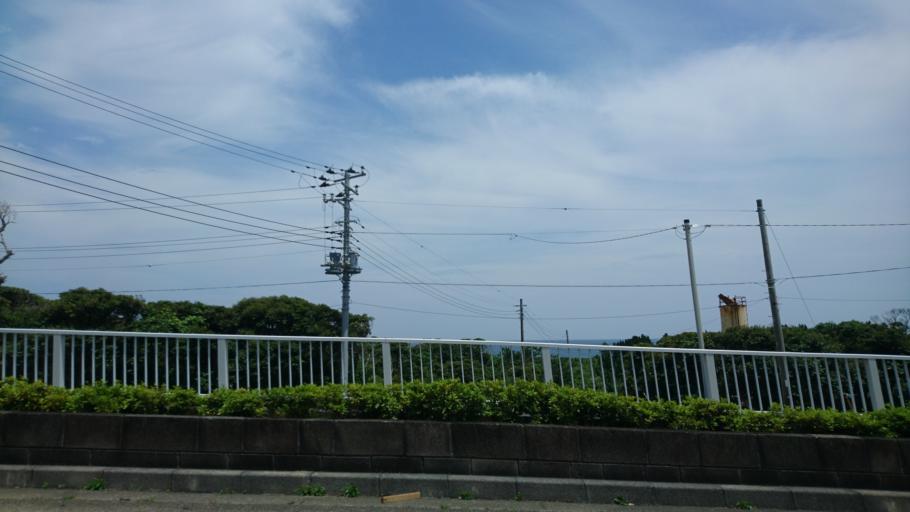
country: JP
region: Shizuoka
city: Shimoda
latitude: 34.3833
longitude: 139.2736
